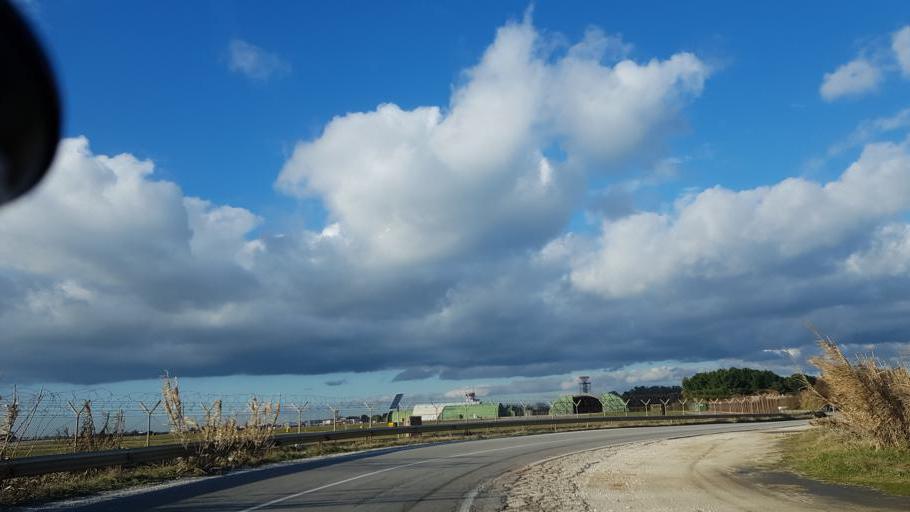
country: IT
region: Apulia
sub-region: Provincia di Brindisi
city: Materdomini
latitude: 40.6635
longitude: 17.9551
